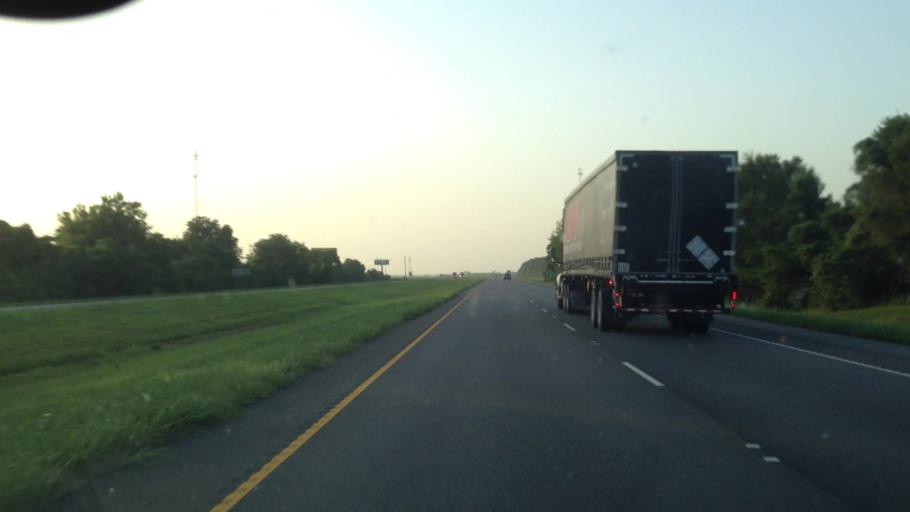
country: US
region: Louisiana
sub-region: Red River Parish
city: Coushatta
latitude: 31.8461
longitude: -93.2939
